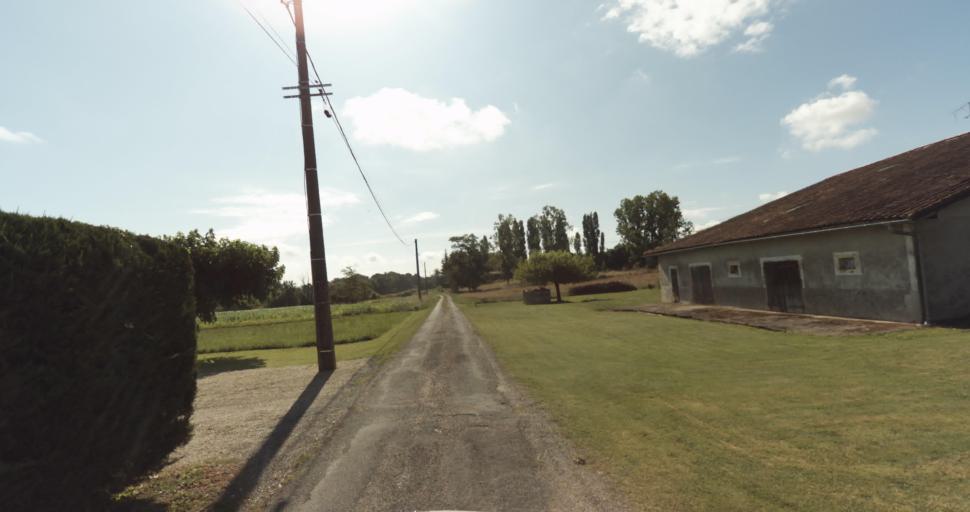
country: FR
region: Aquitaine
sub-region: Departement de la Gironde
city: Bazas
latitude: 44.4249
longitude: -0.2058
